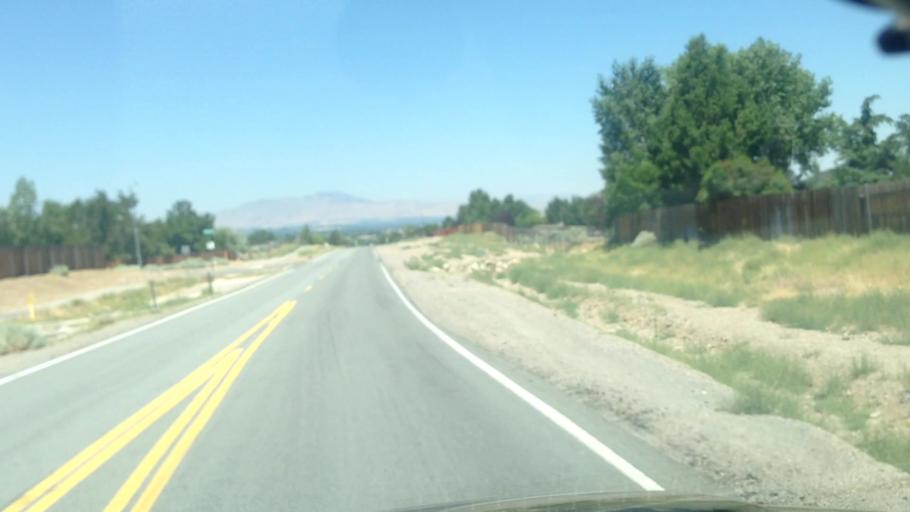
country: US
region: Nevada
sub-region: Storey County
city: Virginia City
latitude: 39.3886
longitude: -119.7282
